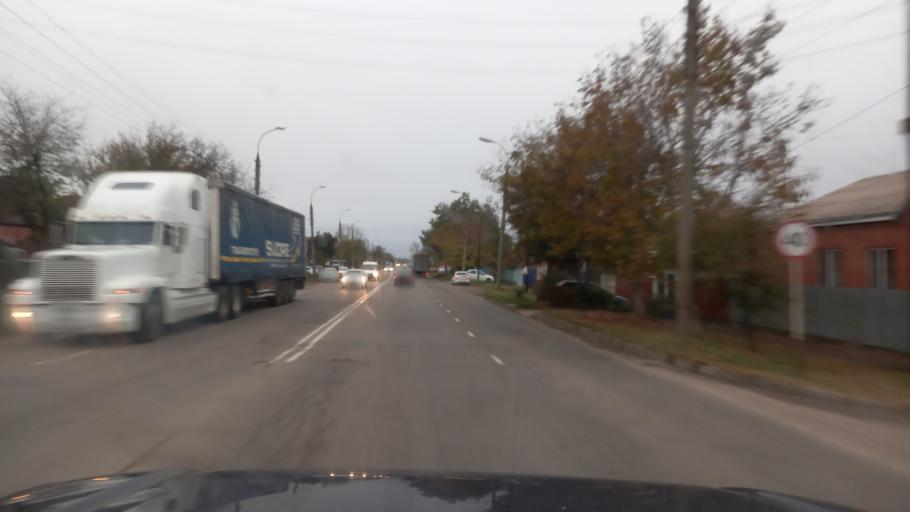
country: RU
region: Adygeya
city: Maykop
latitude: 44.6208
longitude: 40.0768
